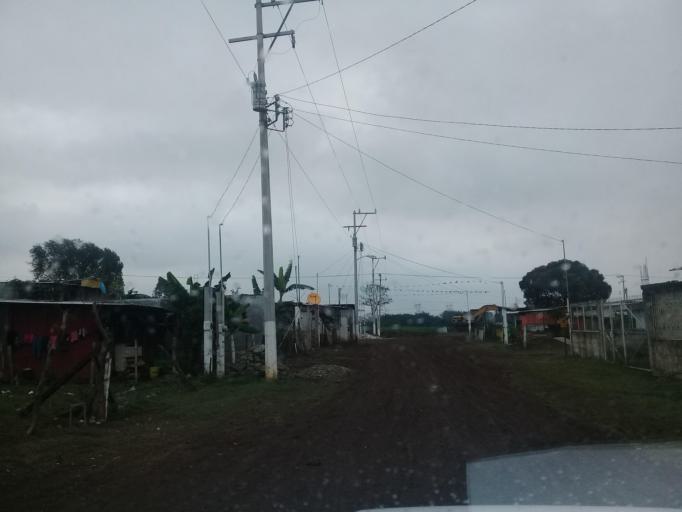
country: MX
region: Veracruz
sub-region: Cordoba
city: San Jose de Tapia
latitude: 18.8520
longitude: -96.9584
